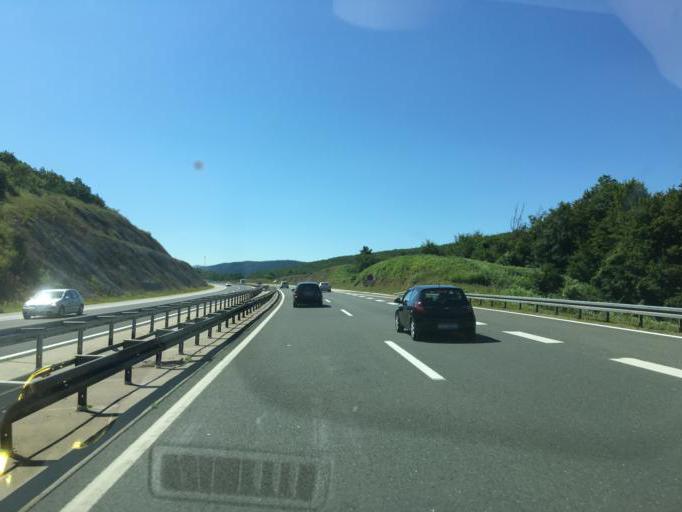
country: HR
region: Licko-Senjska
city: Otocac
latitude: 44.8882
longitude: 15.1945
